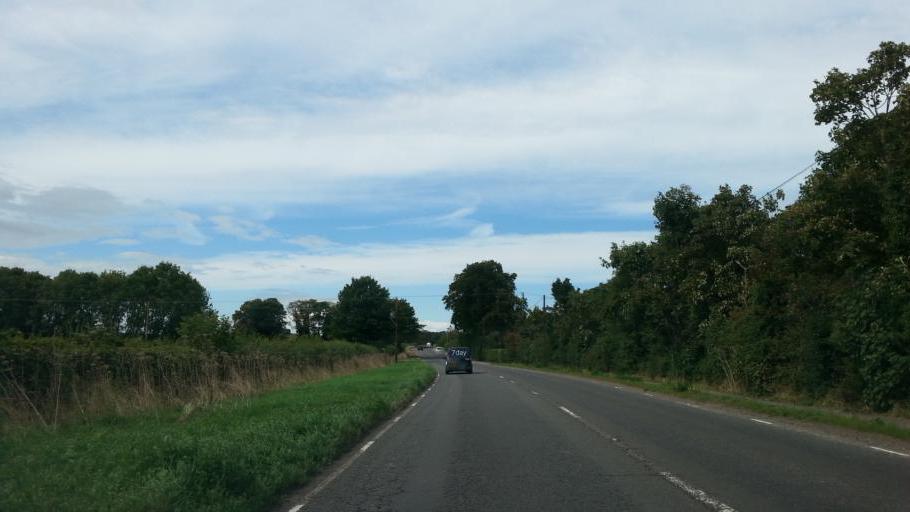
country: GB
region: England
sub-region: Cambridgeshire
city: Sawston
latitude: 52.1428
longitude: 0.1989
